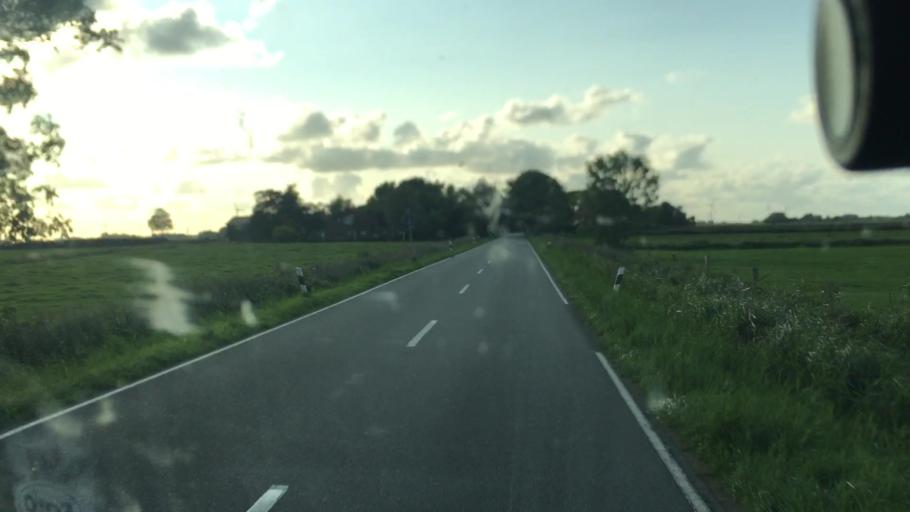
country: DE
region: Lower Saxony
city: Wittmund
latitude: 53.6383
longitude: 7.8258
